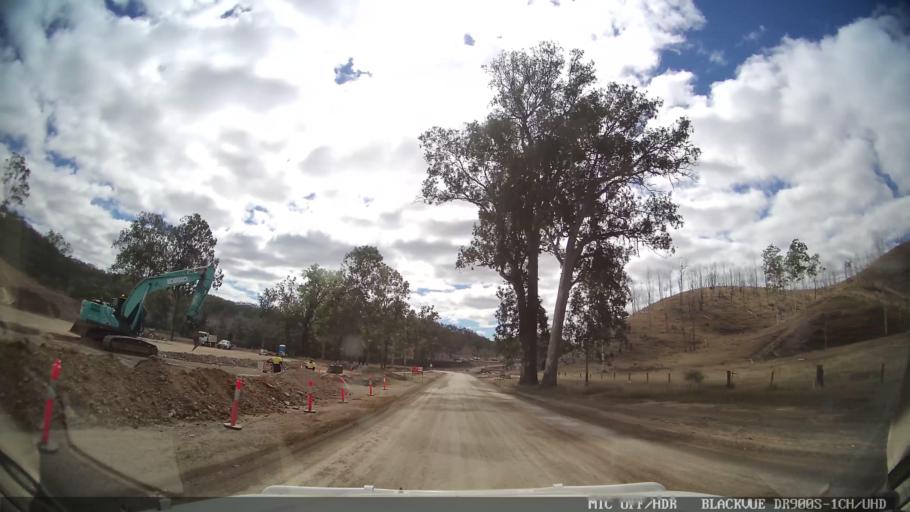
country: AU
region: Queensland
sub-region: Gladstone
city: Toolooa
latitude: -24.6166
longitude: 151.2987
